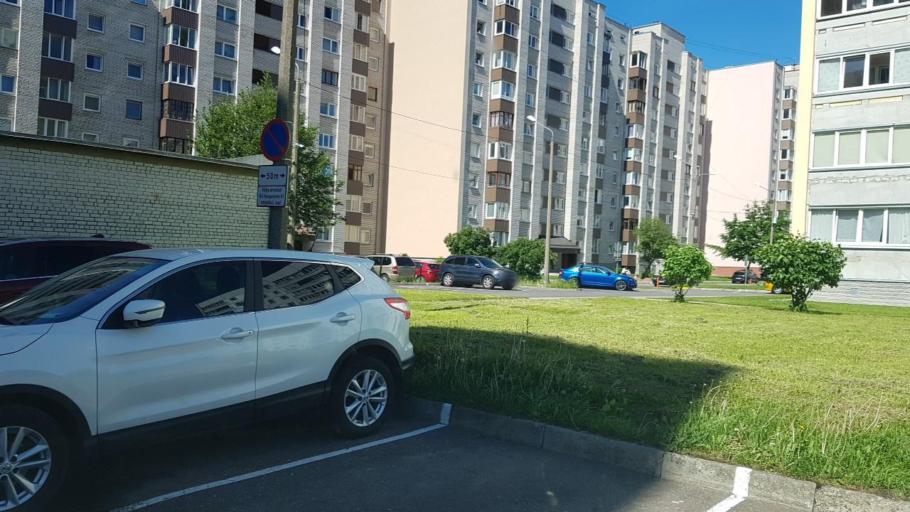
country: EE
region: Ida-Virumaa
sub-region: Narva linn
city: Narva
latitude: 59.3904
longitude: 28.1750
